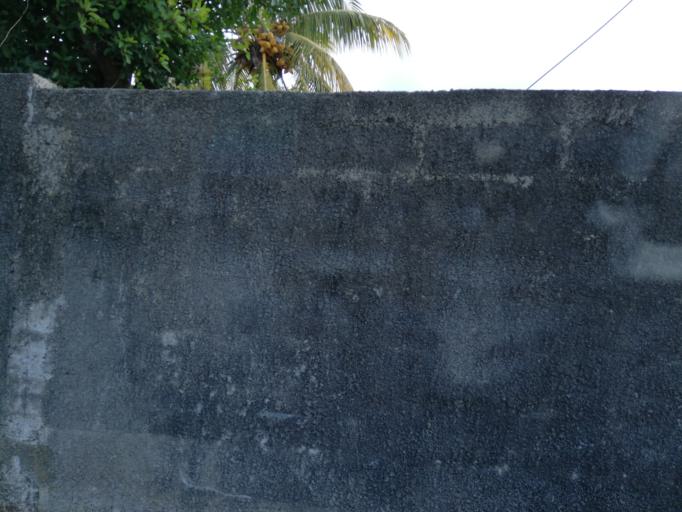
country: MU
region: Plaines Wilhems
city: Ebene
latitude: -20.2335
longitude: 57.4582
